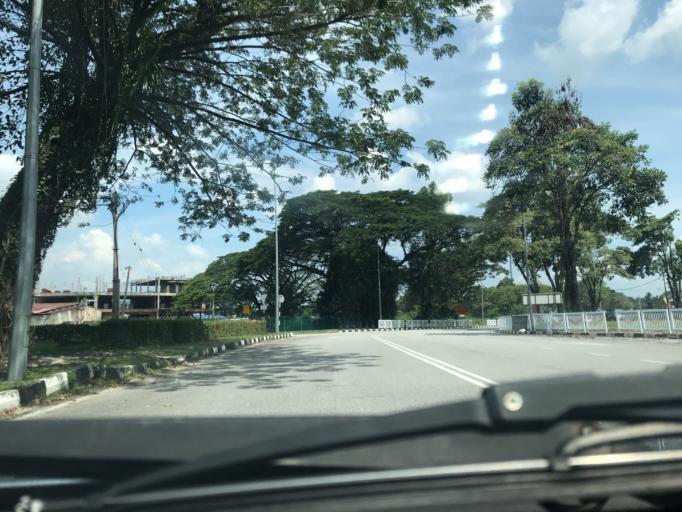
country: MY
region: Perak
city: Ipoh
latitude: 4.6055
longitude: 101.0992
